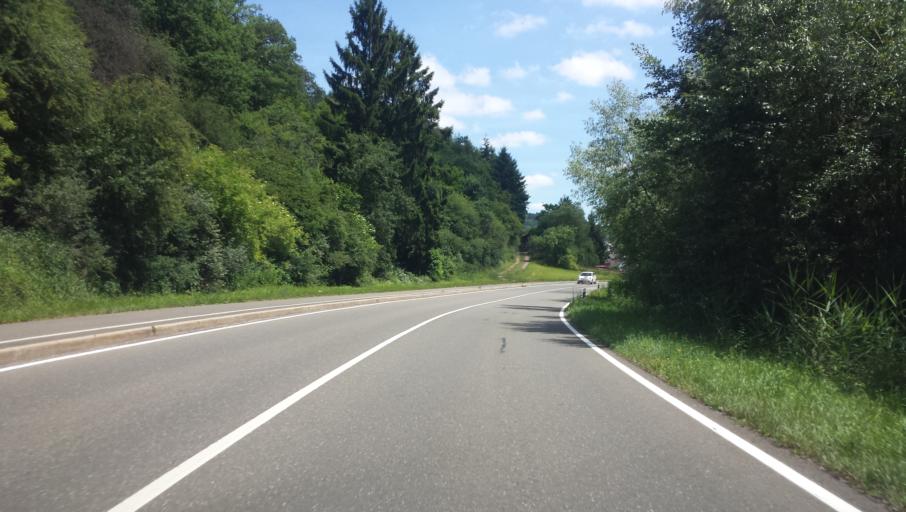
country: DE
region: Rheinland-Pfalz
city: Waldhambach
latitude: 49.1657
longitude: 7.9820
